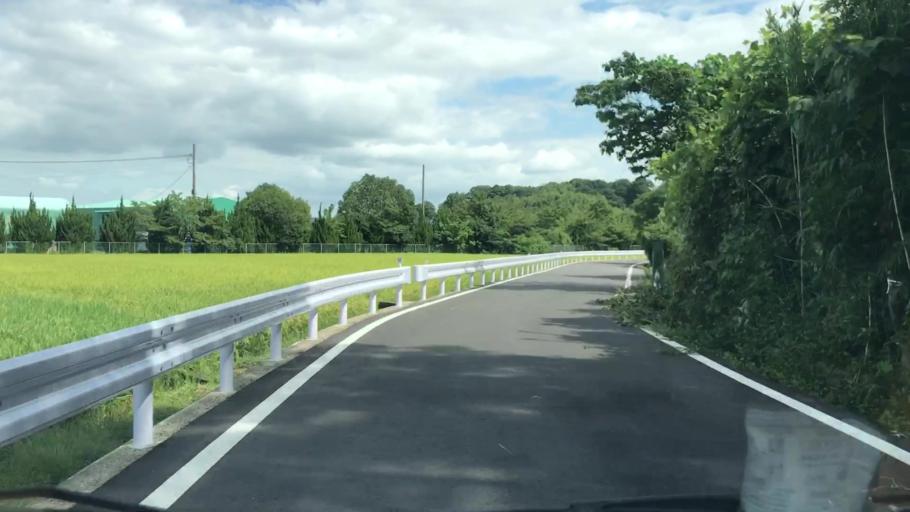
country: JP
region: Saga Prefecture
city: Saga-shi
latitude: 33.2310
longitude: 130.1747
